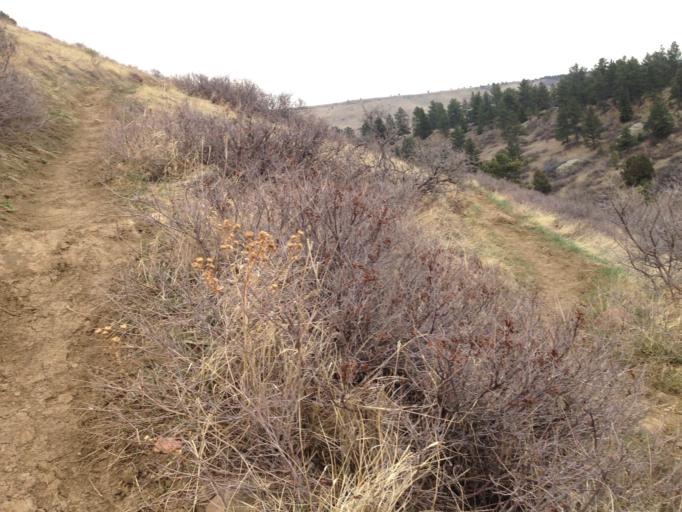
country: US
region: Colorado
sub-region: Boulder County
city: Boulder
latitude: 39.9437
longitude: -105.2707
